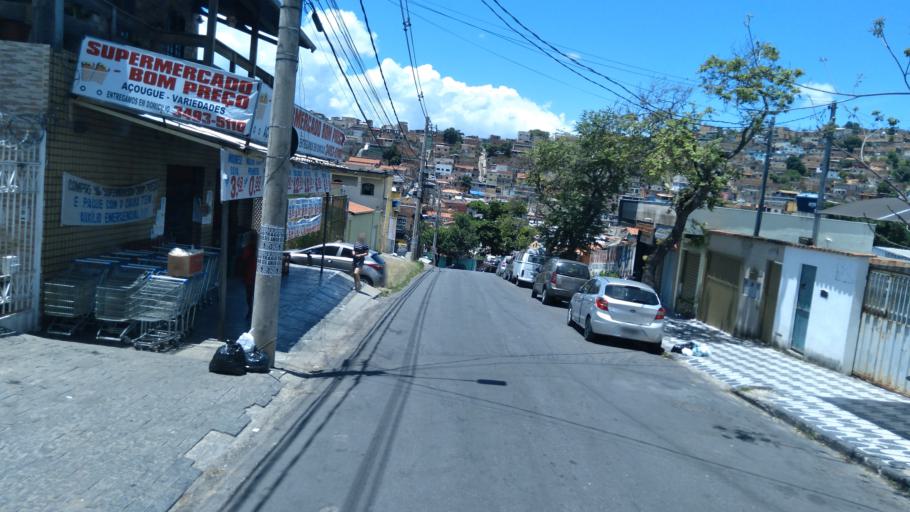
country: BR
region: Minas Gerais
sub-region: Santa Luzia
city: Santa Luzia
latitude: -19.8339
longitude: -43.8899
